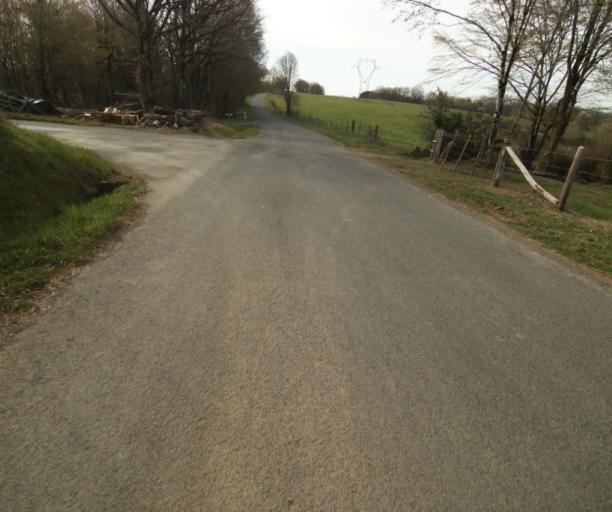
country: FR
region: Limousin
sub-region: Departement de la Correze
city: Seilhac
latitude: 45.4108
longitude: 1.7839
